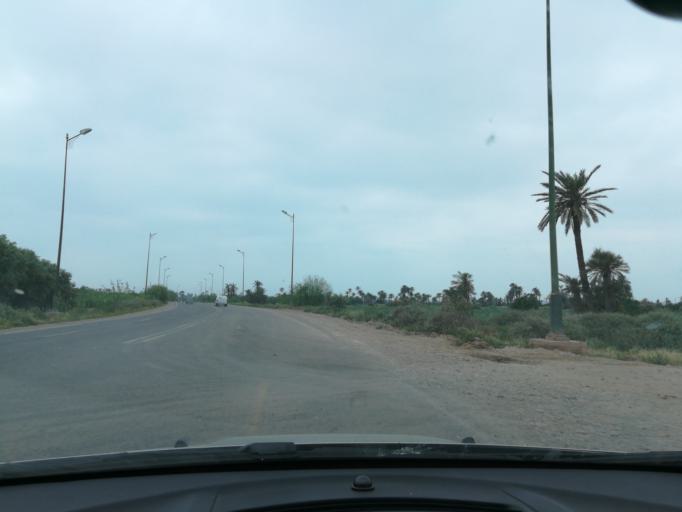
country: MA
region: Marrakech-Tensift-Al Haouz
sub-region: Marrakech
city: Marrakesh
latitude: 31.6902
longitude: -8.0062
